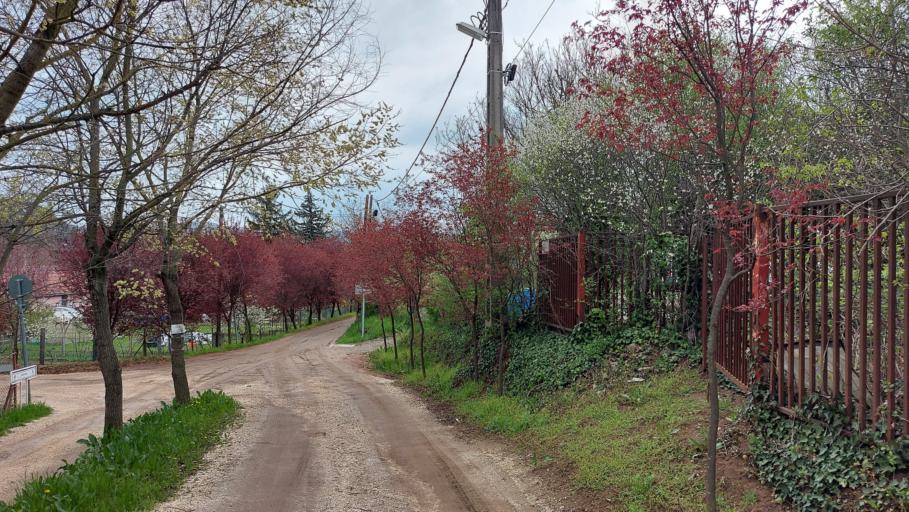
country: HU
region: Pest
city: Budaors
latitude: 47.4361
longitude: 18.9539
